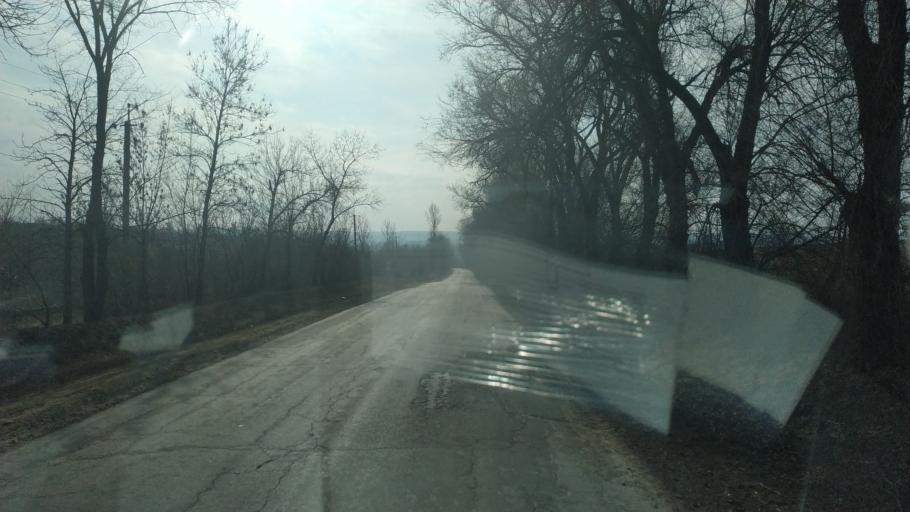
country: MD
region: Chisinau
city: Singera
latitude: 46.9321
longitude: 29.0473
